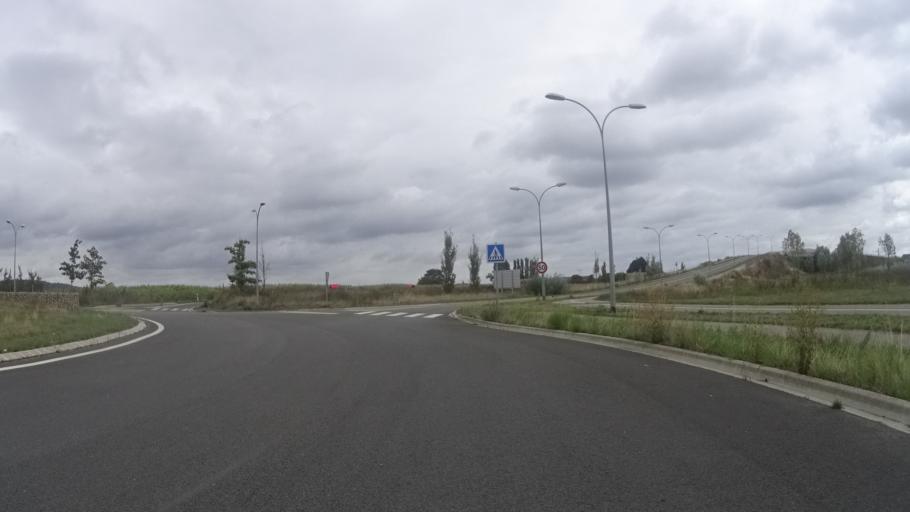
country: FR
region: Picardie
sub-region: Departement de l'Oise
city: Dreslincourt
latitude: 49.5103
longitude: 2.9365
